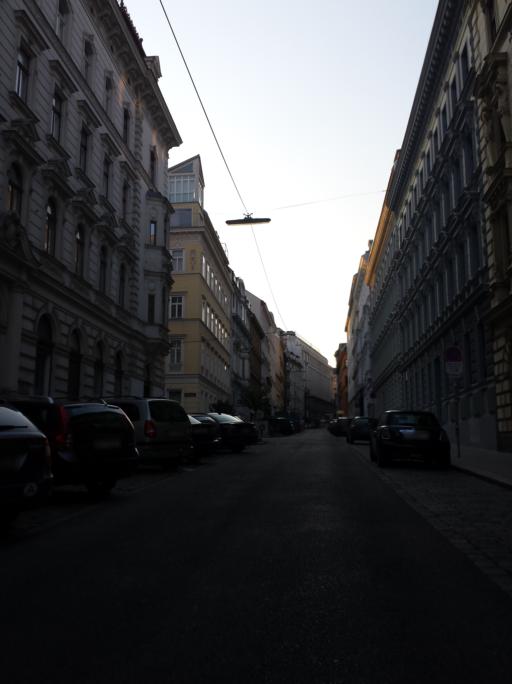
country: AT
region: Vienna
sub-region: Wien Stadt
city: Vienna
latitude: 48.1957
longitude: 16.3509
